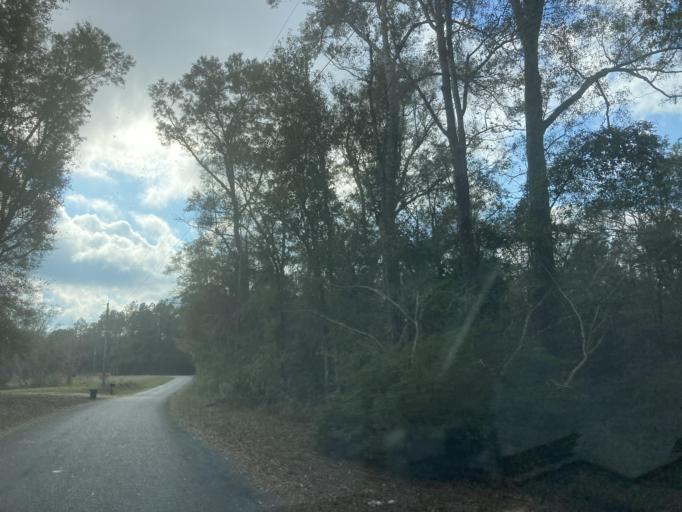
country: US
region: Mississippi
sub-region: Stone County
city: Wiggins
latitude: 30.8010
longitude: -89.1074
